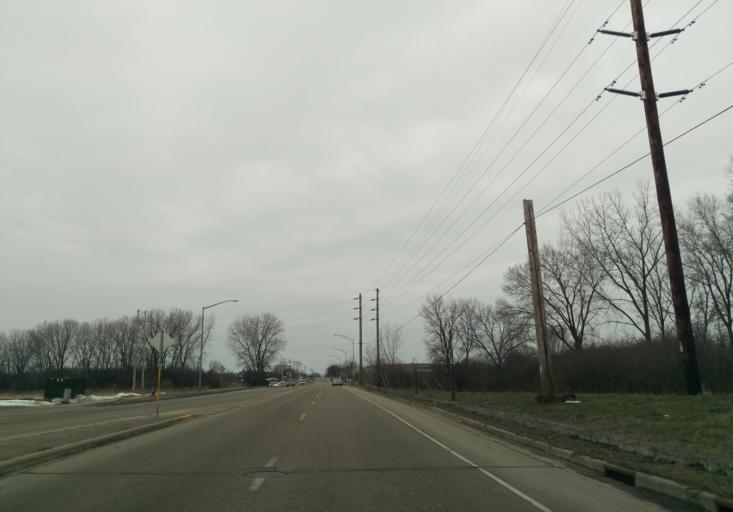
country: US
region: Wisconsin
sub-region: Dane County
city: Monona
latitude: 43.1211
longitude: -89.3011
